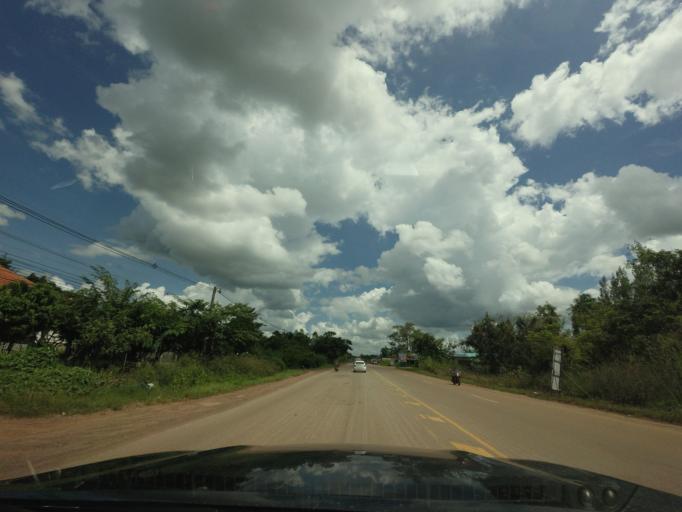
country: TH
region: Changwat Udon Thani
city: Ban Dung
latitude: 17.6786
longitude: 103.2411
